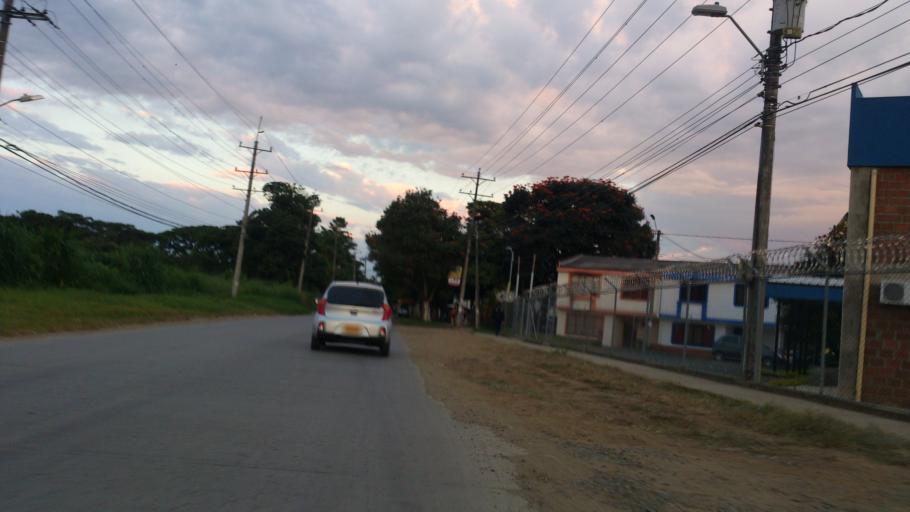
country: CO
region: Valle del Cauca
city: Jamundi
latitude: 3.2569
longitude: -76.5492
